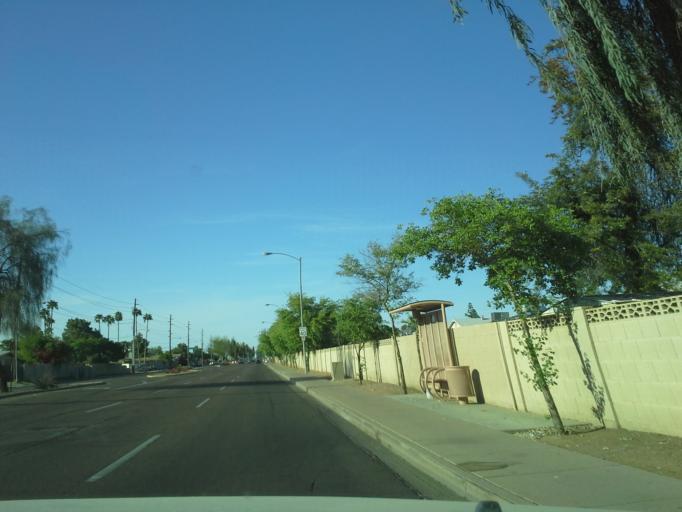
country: US
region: Arizona
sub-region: Maricopa County
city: Glendale
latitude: 33.5754
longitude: -112.1341
